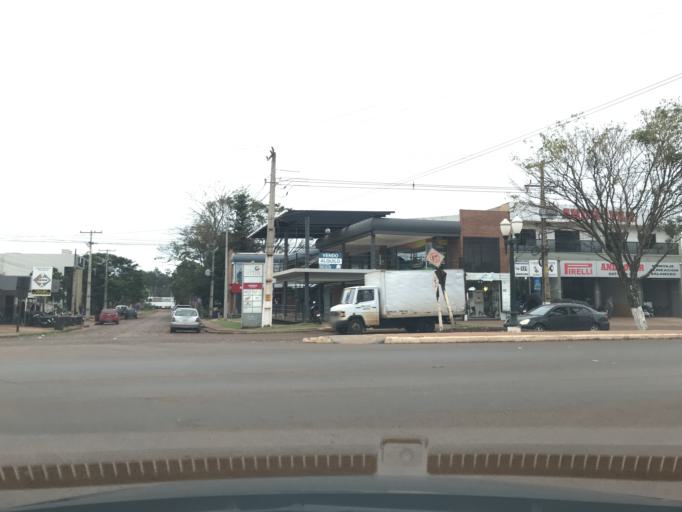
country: PY
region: Canindeyu
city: Colonia Catuete
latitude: -24.2469
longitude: -54.7602
